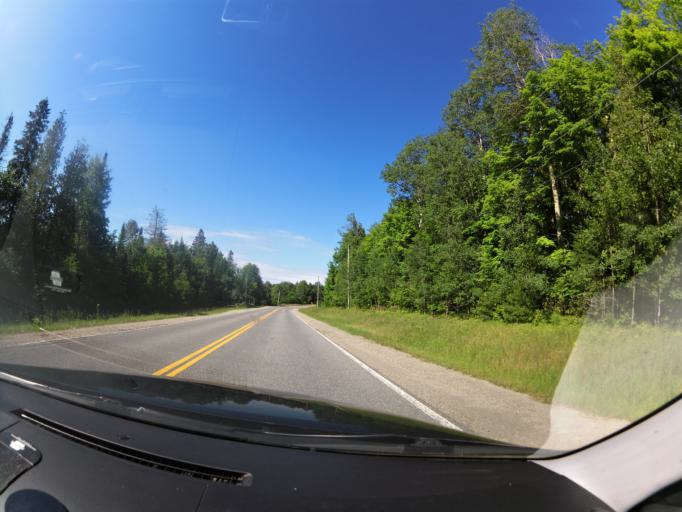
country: CA
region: Ontario
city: Carleton Place
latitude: 45.1201
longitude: -76.3498
